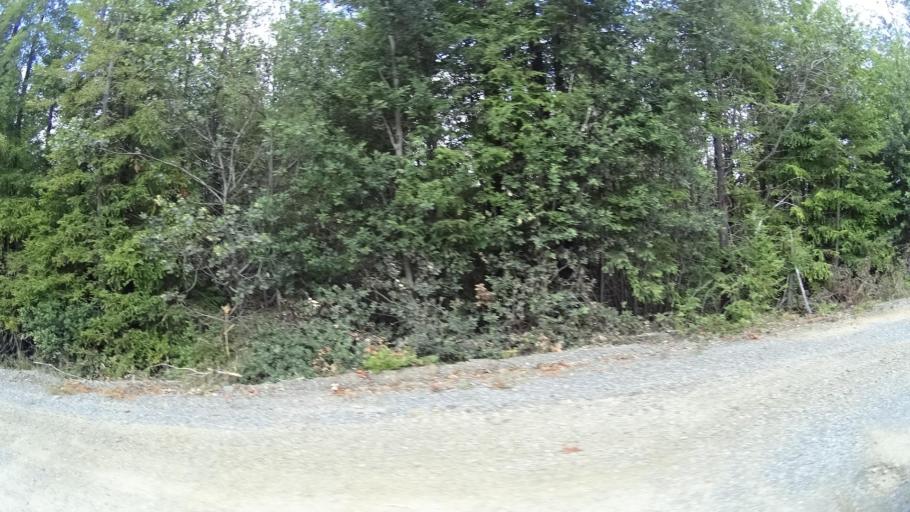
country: US
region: California
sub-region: Humboldt County
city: Blue Lake
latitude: 40.7710
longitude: -123.9579
